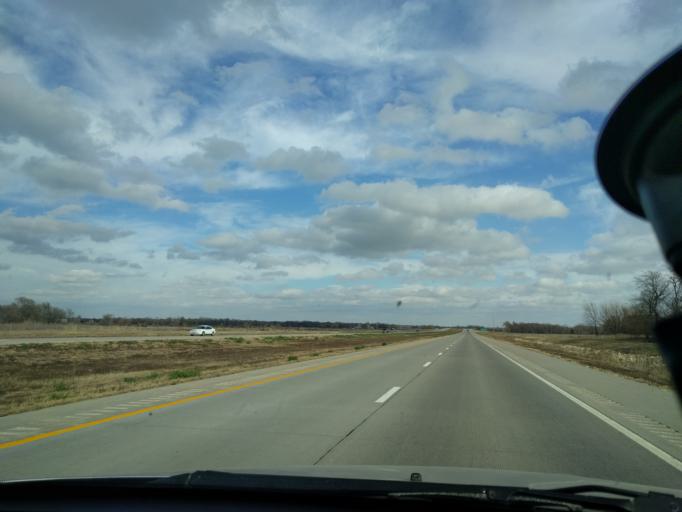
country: US
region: Kansas
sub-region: Reno County
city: Buhler
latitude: 38.1491
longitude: -97.8595
